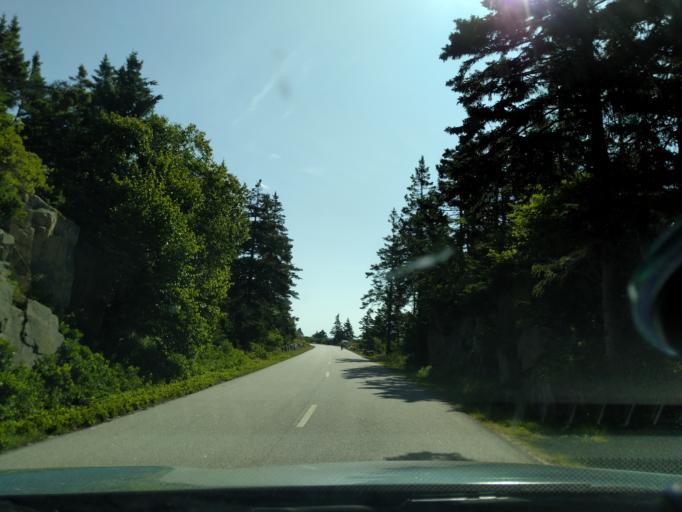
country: US
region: Maine
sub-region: Hancock County
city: Gouldsboro
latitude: 44.3383
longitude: -68.0504
